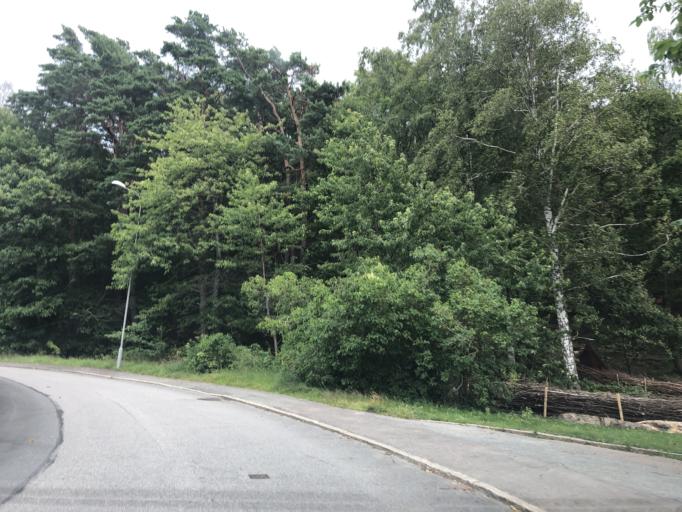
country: SE
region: Vaestra Goetaland
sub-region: Goteborg
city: Majorna
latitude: 57.7362
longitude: 11.9156
